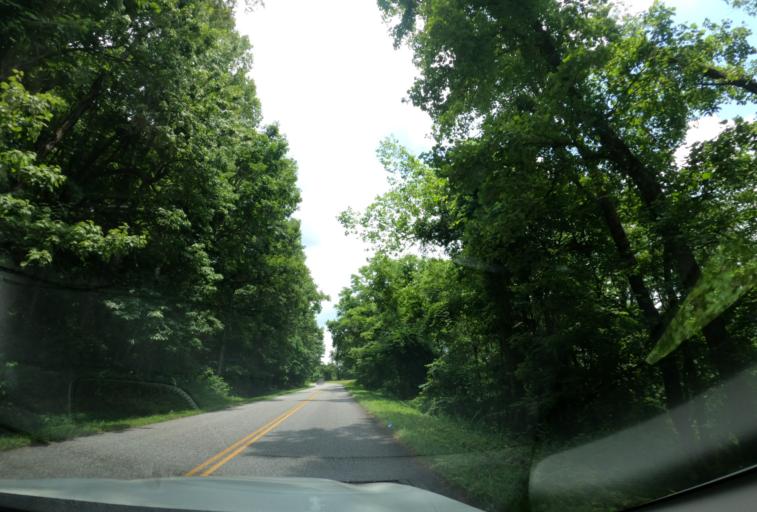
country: US
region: North Carolina
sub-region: Buncombe County
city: Bent Creek
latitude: 35.4735
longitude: -82.6199
